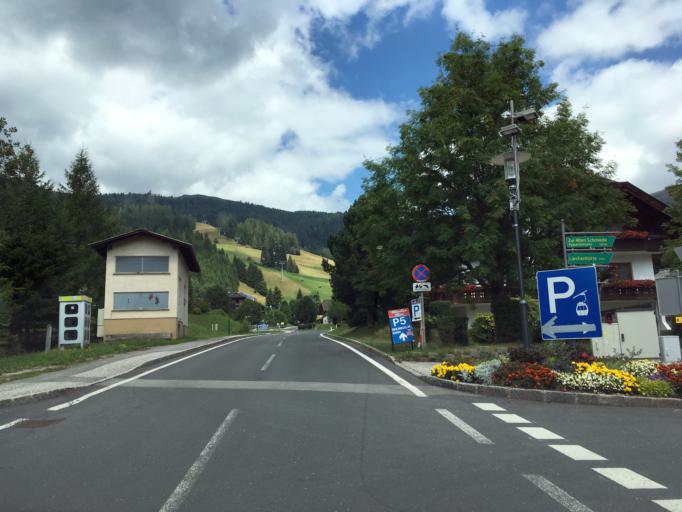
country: AT
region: Carinthia
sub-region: Politischer Bezirk Spittal an der Drau
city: Kleinkirchheim
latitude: 46.8420
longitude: 13.7658
